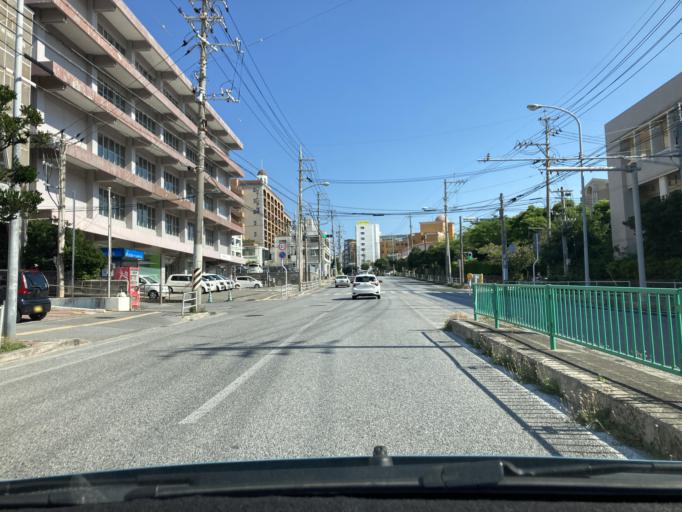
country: JP
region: Okinawa
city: Naha-shi
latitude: 26.2069
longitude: 127.6939
